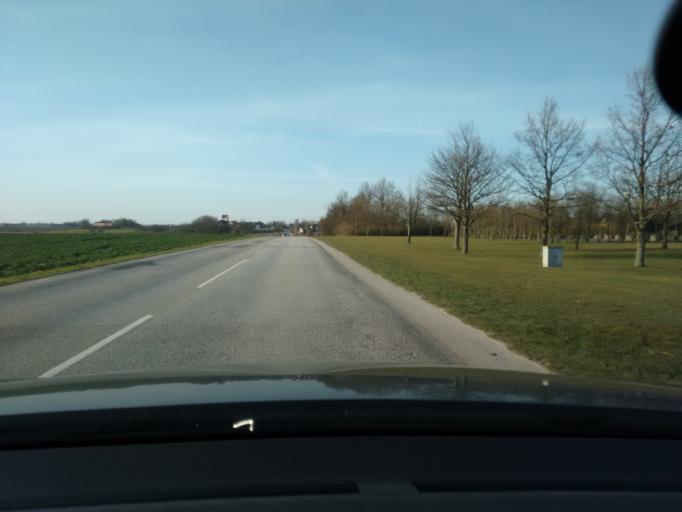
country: SE
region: Skane
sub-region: Lunds Kommun
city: Lund
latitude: 55.7356
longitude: 13.1751
